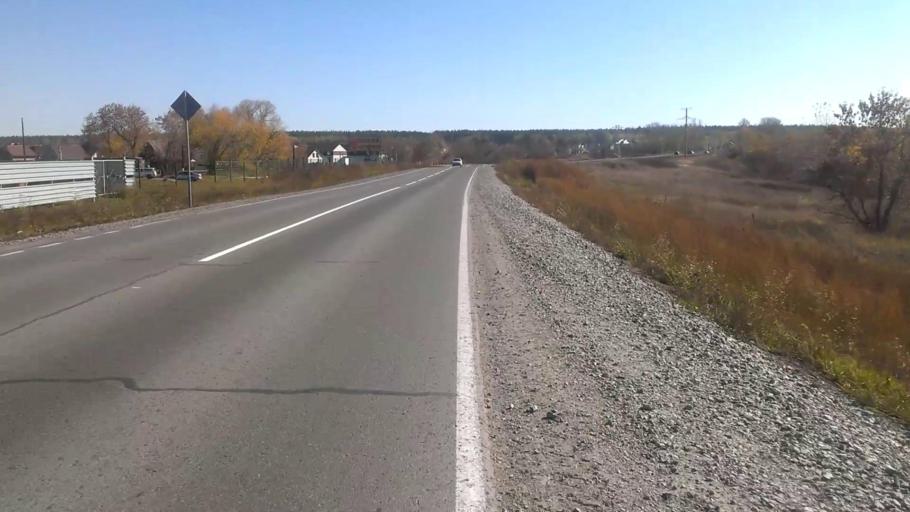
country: RU
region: Altai Krai
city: Sannikovo
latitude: 53.3131
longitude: 83.9632
